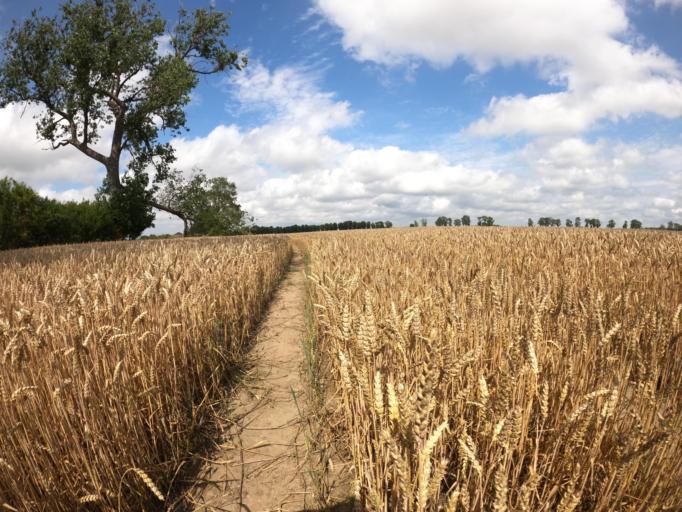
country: PL
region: West Pomeranian Voivodeship
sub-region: Powiat szczecinecki
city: Grzmiaca
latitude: 53.8080
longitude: 16.4705
